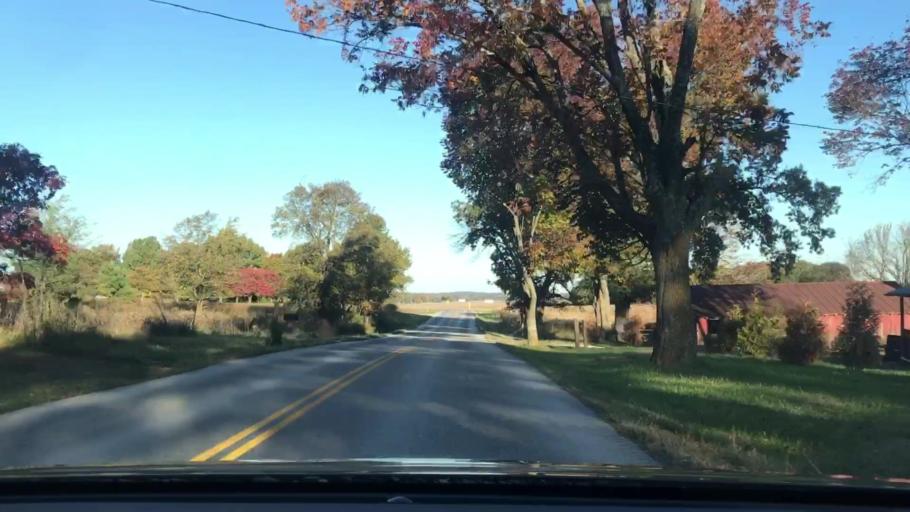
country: US
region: Kentucky
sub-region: Logan County
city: Auburn
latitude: 36.8272
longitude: -86.6758
